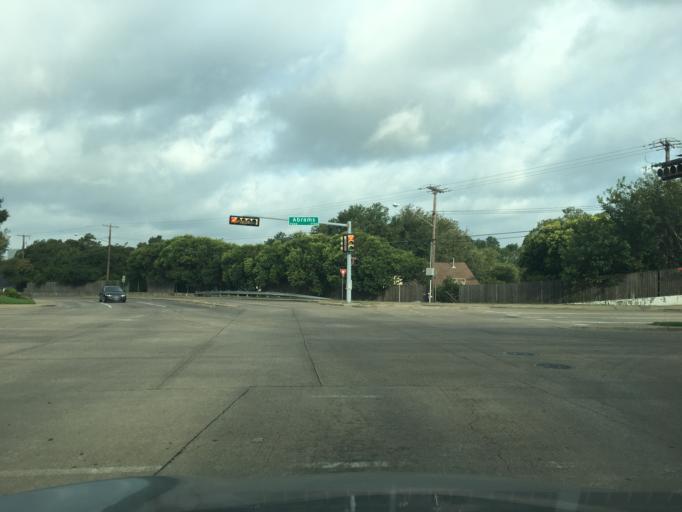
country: US
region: Texas
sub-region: Dallas County
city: Richardson
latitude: 32.8860
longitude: -96.7406
